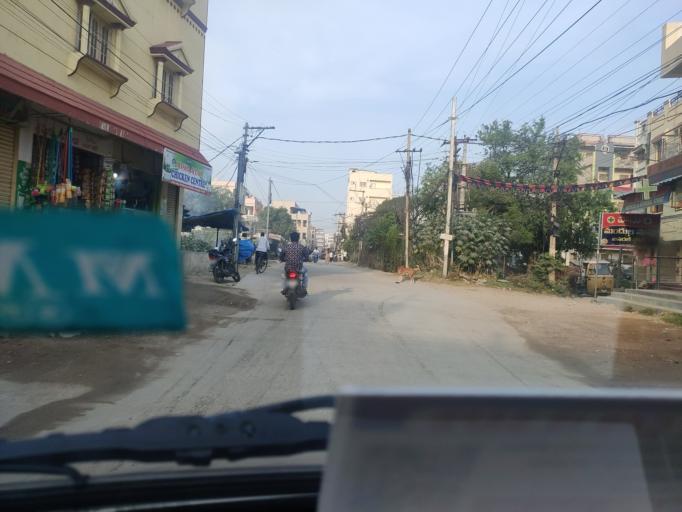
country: IN
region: Telangana
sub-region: Rangareddi
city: Kukatpalli
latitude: 17.5049
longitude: 78.4142
